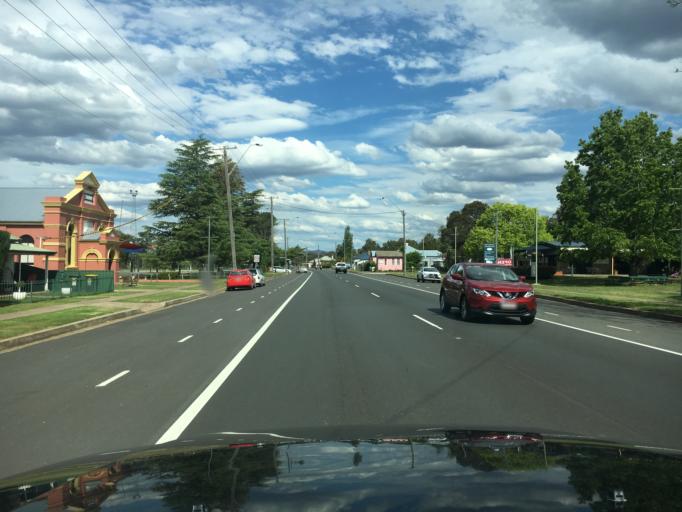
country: AU
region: New South Wales
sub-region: Liverpool Plains
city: Quirindi
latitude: -31.7631
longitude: 150.8338
